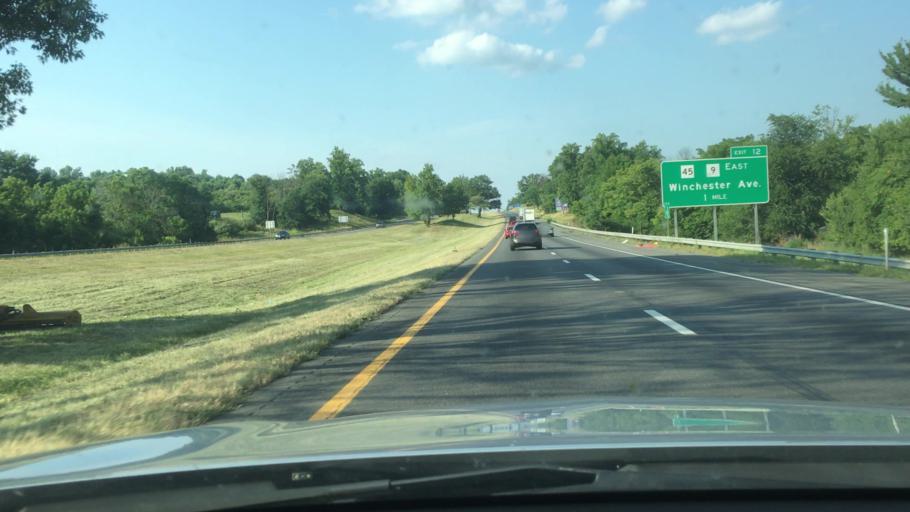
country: US
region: West Virginia
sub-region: Berkeley County
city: Martinsburg
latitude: 39.4283
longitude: -77.9987
